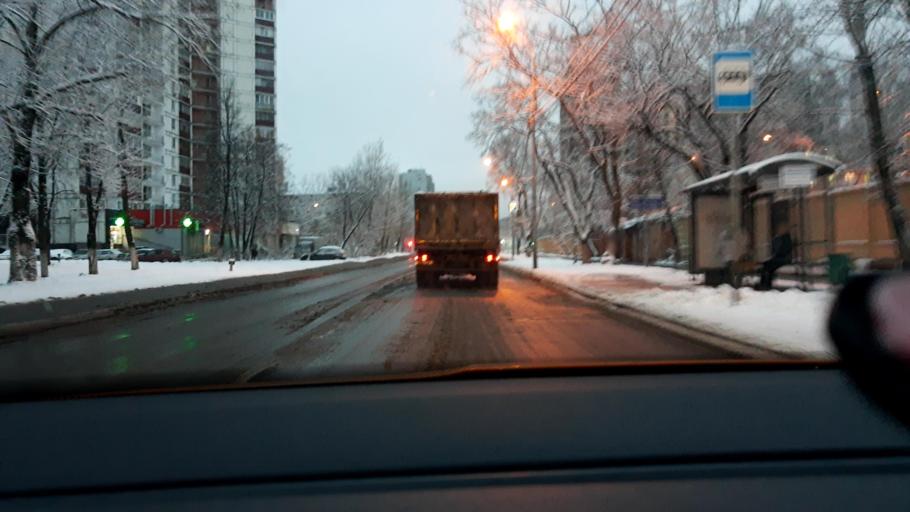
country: RU
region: Moscow
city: Lyublino
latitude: 55.6821
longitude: 37.7668
